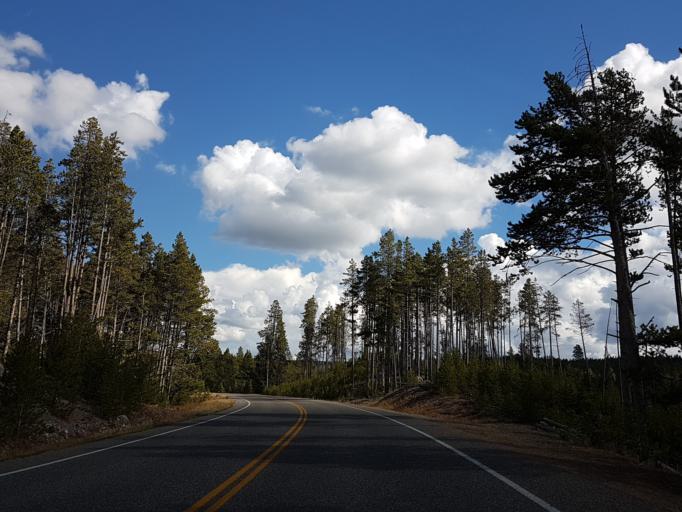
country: US
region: Montana
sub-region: Gallatin County
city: West Yellowstone
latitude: 44.5338
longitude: -110.8218
